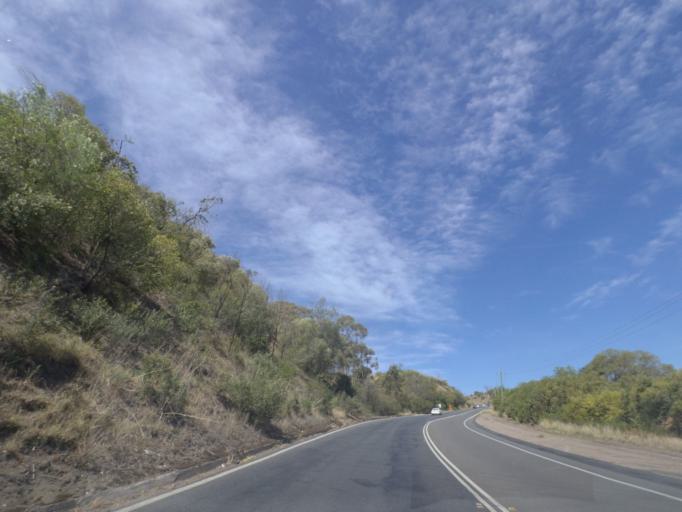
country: AU
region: New South Wales
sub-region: Wollondilly
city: Picton
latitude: -34.1529
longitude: 150.6603
